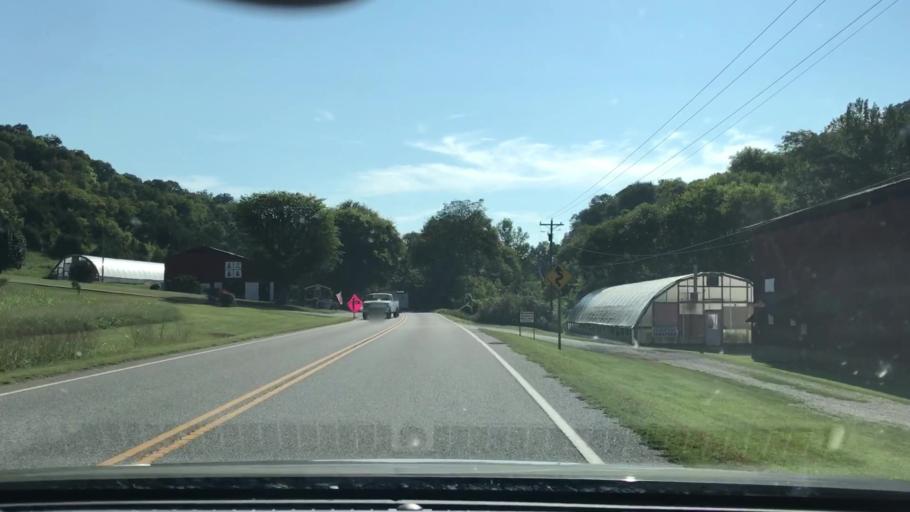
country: US
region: Tennessee
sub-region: Smith County
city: Carthage
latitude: 36.3520
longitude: -85.8914
